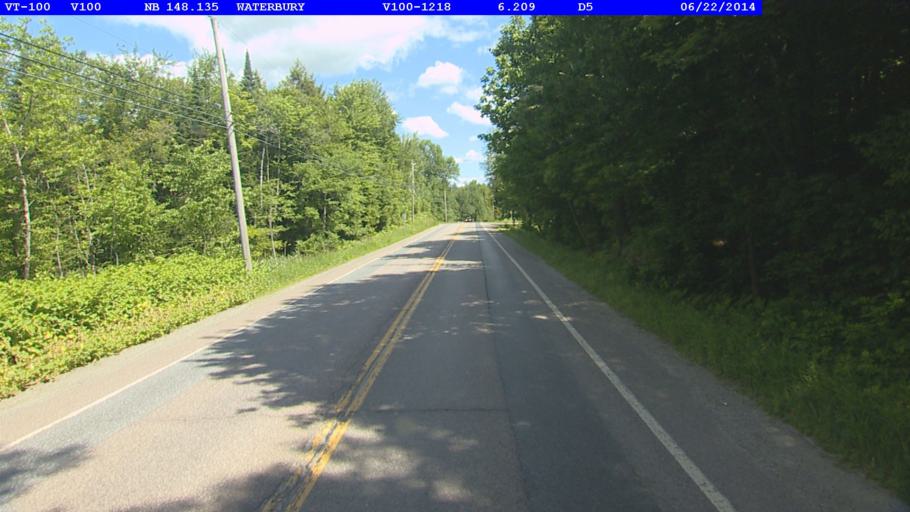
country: US
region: Vermont
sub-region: Washington County
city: Waterbury
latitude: 44.4178
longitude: -72.7227
